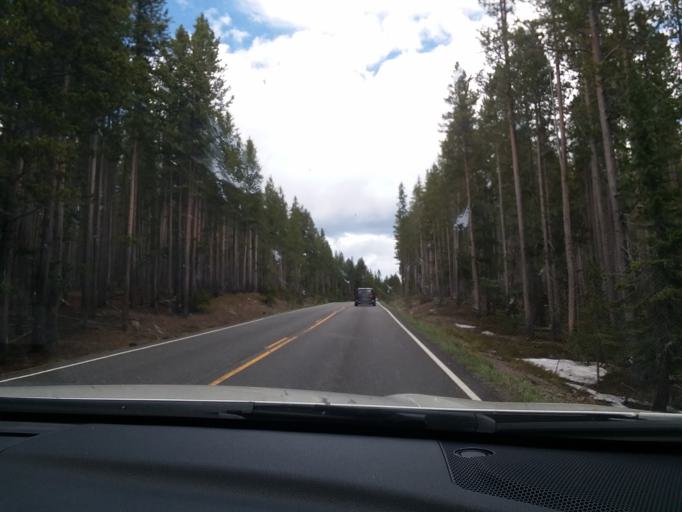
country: US
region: Idaho
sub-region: Teton County
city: Driggs
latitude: 44.1871
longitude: -110.6574
